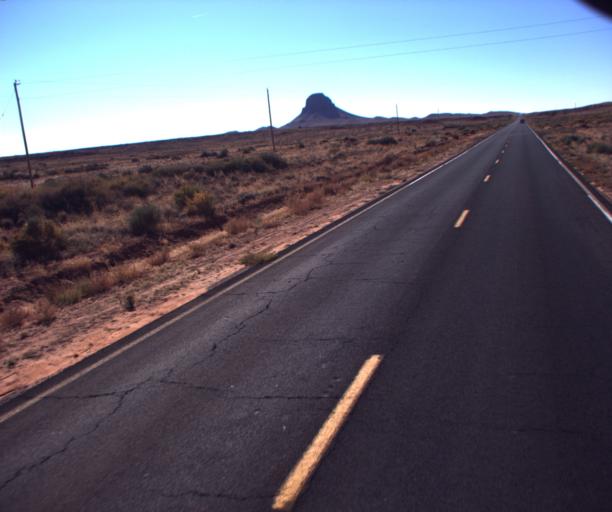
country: US
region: Arizona
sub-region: Navajo County
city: Dilkon
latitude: 35.3322
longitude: -110.4236
